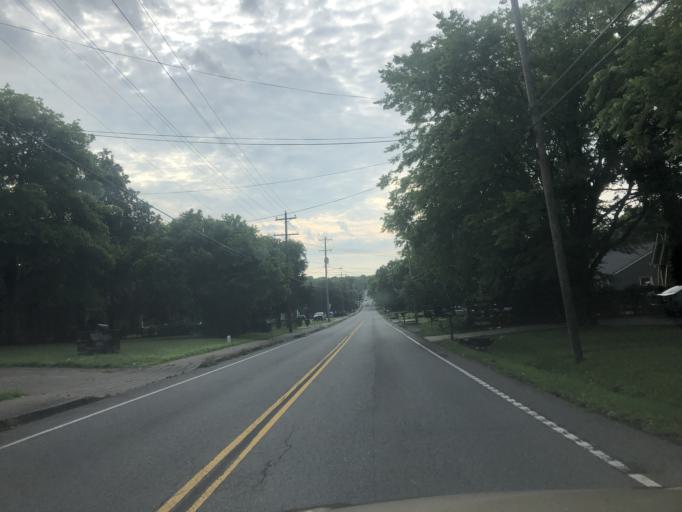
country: US
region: Tennessee
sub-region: Davidson County
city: Goodlettsville
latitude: 36.2560
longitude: -86.7126
